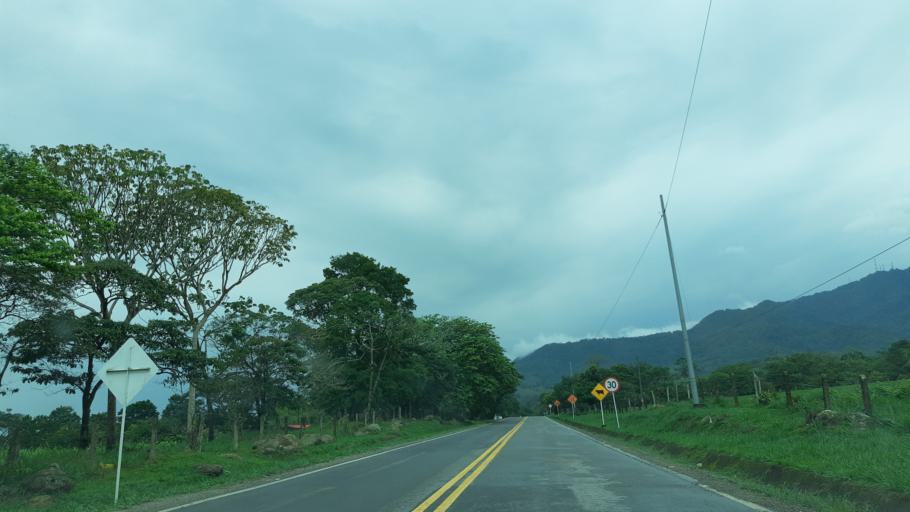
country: CO
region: Casanare
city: Monterrey
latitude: 4.8424
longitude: -72.9495
